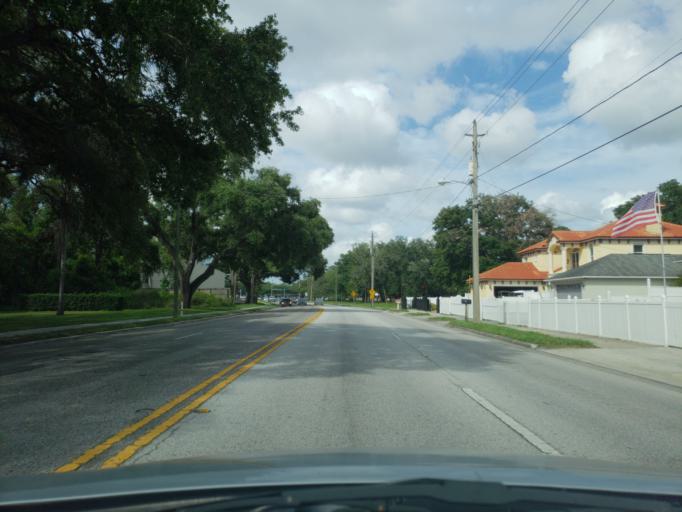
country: US
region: Florida
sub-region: Hillsborough County
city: Egypt Lake-Leto
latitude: 28.0085
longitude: -82.4909
